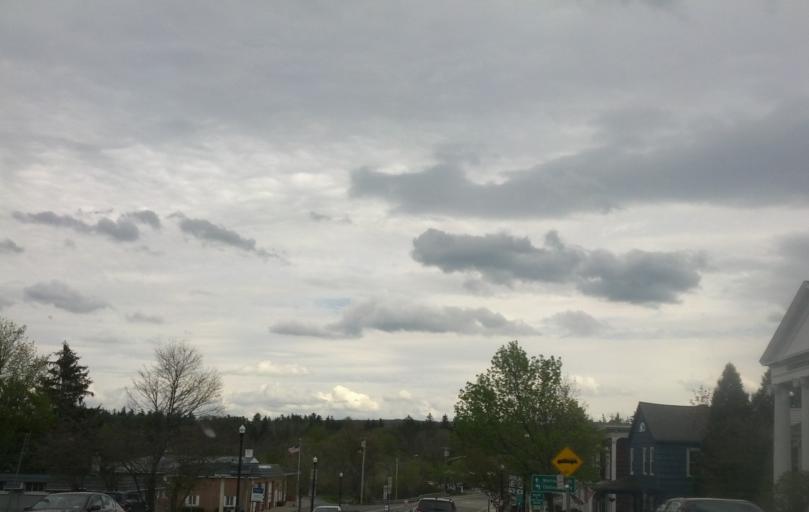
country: US
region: New York
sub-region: Madison County
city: Cazenovia
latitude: 42.9298
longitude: -75.8524
